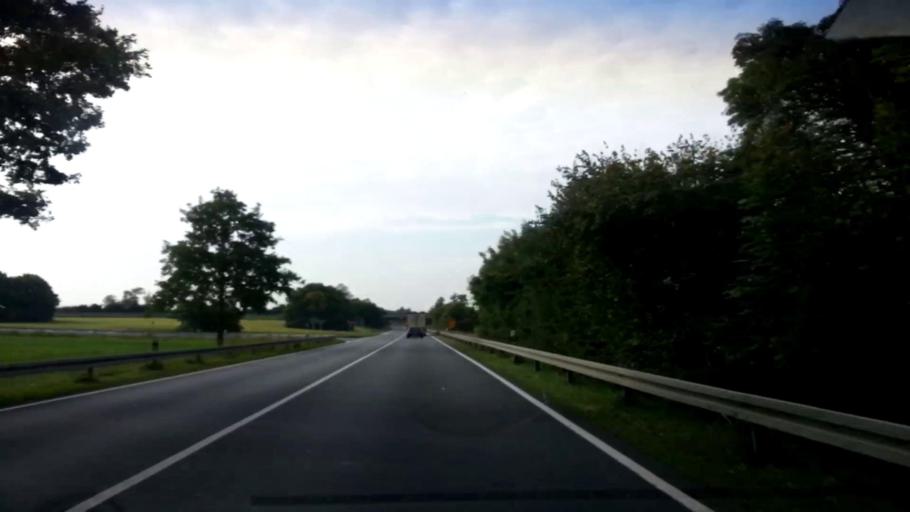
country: DE
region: Bavaria
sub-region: Regierungsbezirk Unterfranken
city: Wiesentheid
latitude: 49.8008
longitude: 10.3583
